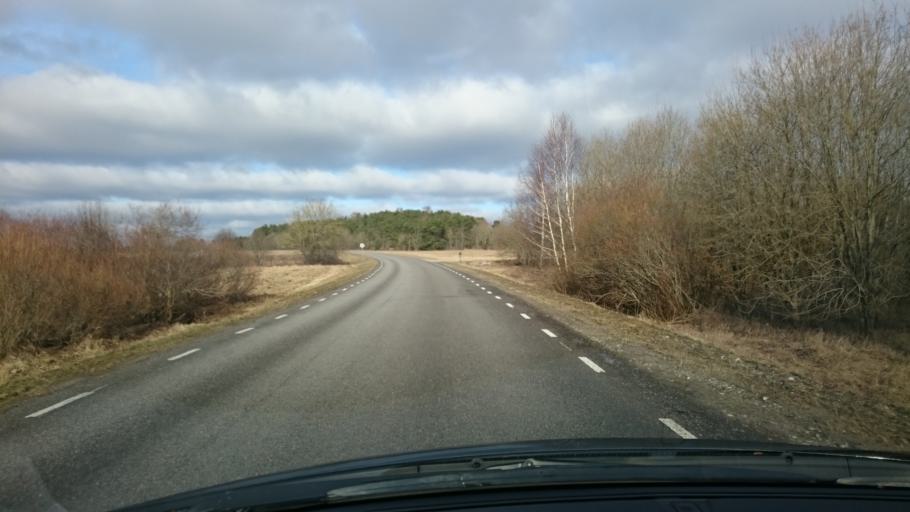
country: EE
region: Harju
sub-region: Keila linn
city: Keila
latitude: 59.3385
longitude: 24.3713
